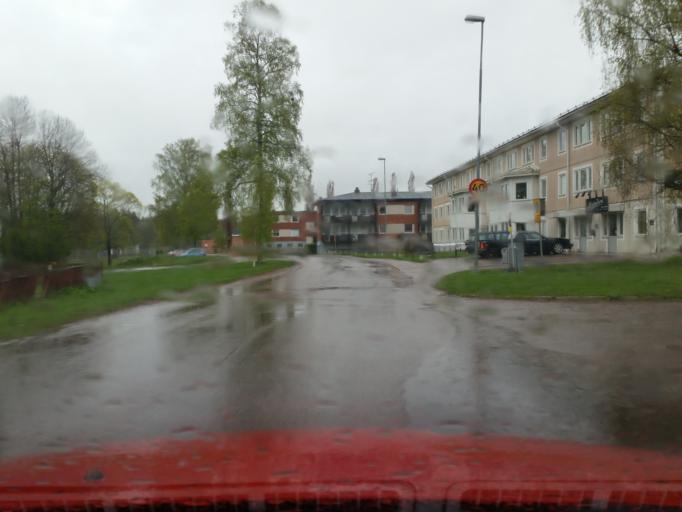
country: SE
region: Dalarna
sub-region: Saters Kommun
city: Saeter
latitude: 60.3480
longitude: 15.7543
